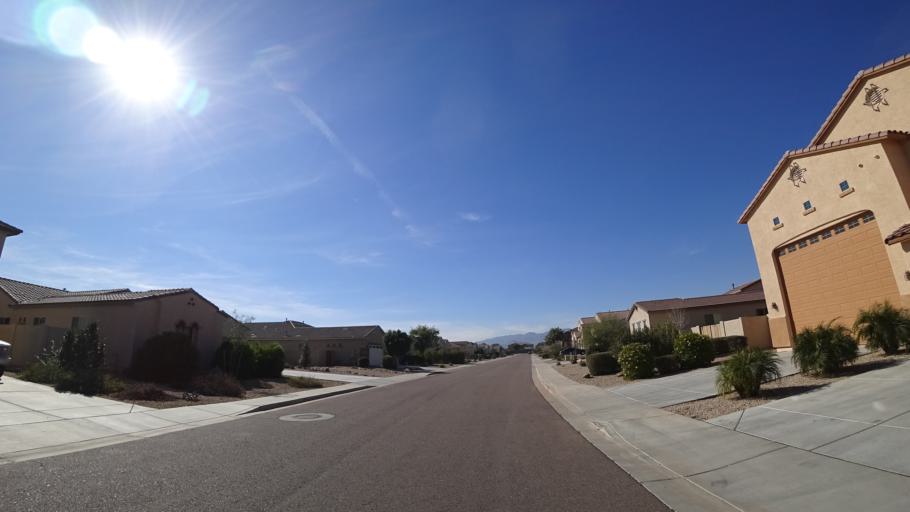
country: US
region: Arizona
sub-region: Maricopa County
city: Citrus Park
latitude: 33.5140
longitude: -112.4578
